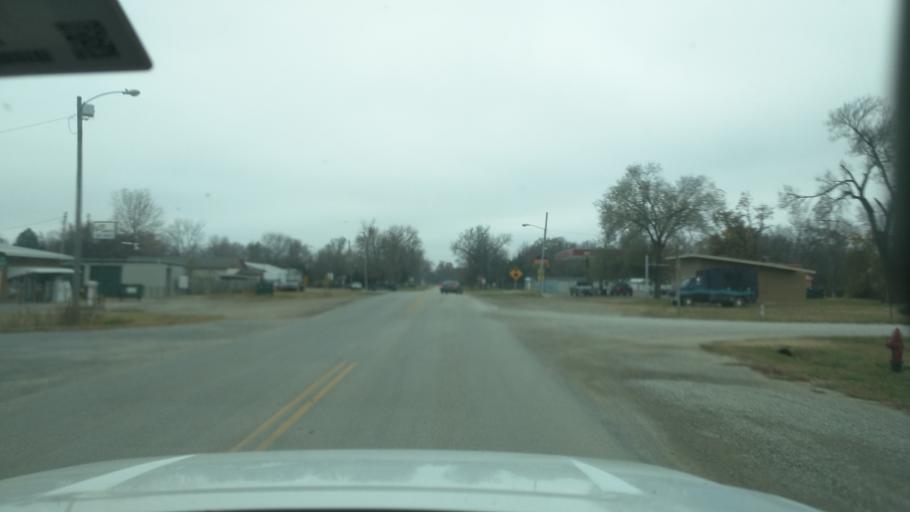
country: US
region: Kansas
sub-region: Lyon County
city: Emporia
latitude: 38.5051
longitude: -96.2623
